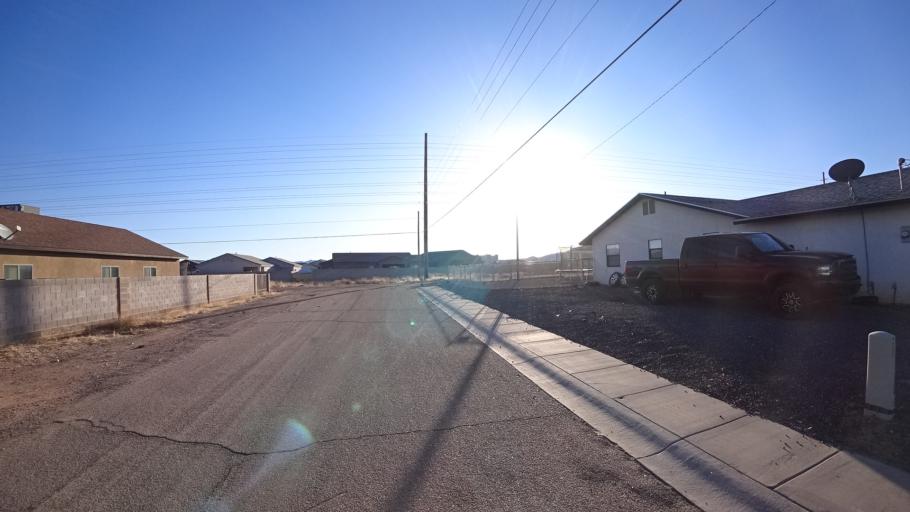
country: US
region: Arizona
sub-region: Mohave County
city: New Kingman-Butler
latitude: 35.2211
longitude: -113.9941
